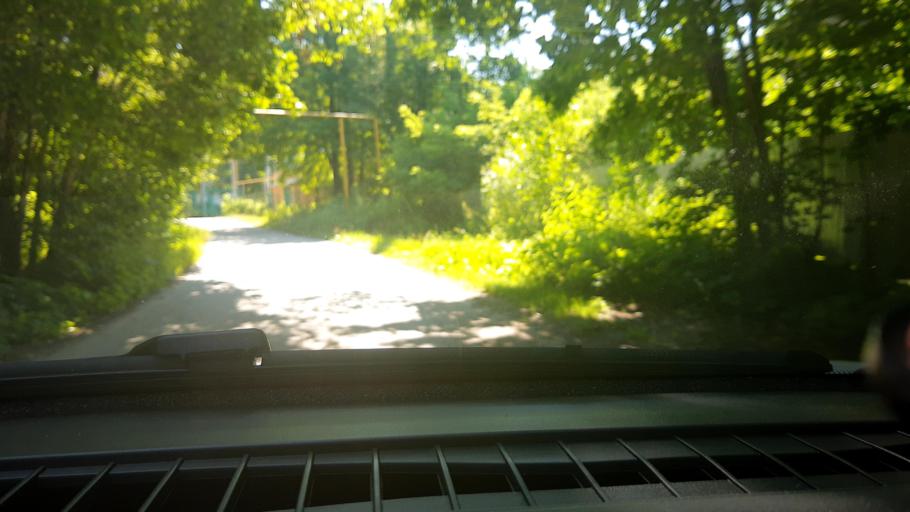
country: RU
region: Nizjnij Novgorod
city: Afonino
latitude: 56.2637
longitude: 44.2068
